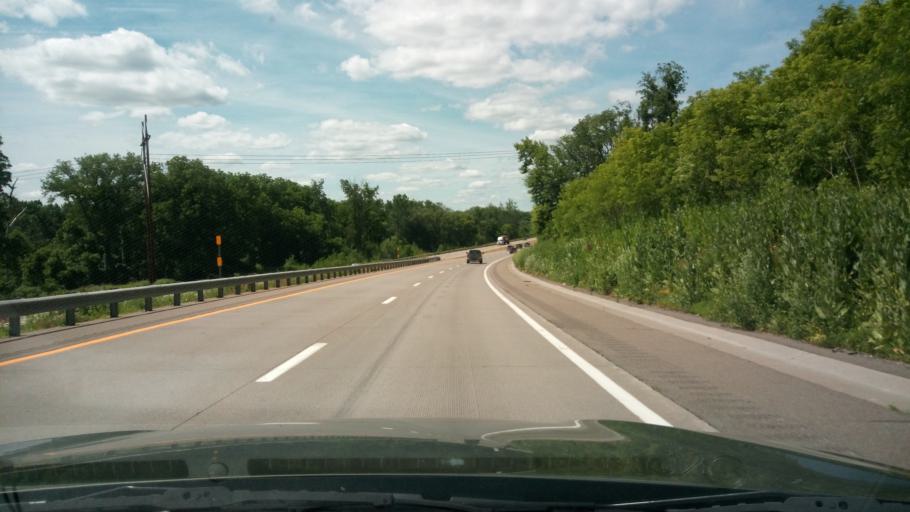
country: US
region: New York
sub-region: Chemung County
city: Elmira
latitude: 42.0580
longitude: -76.7565
